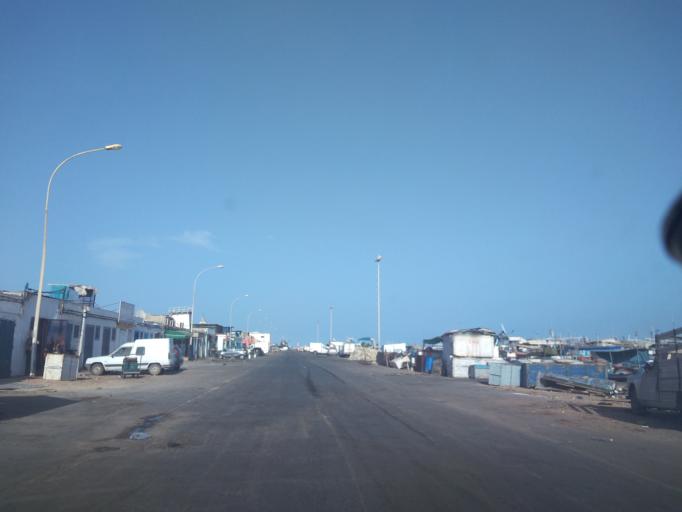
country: TN
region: Safaqis
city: Sfax
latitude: 34.7131
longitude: 10.7621
